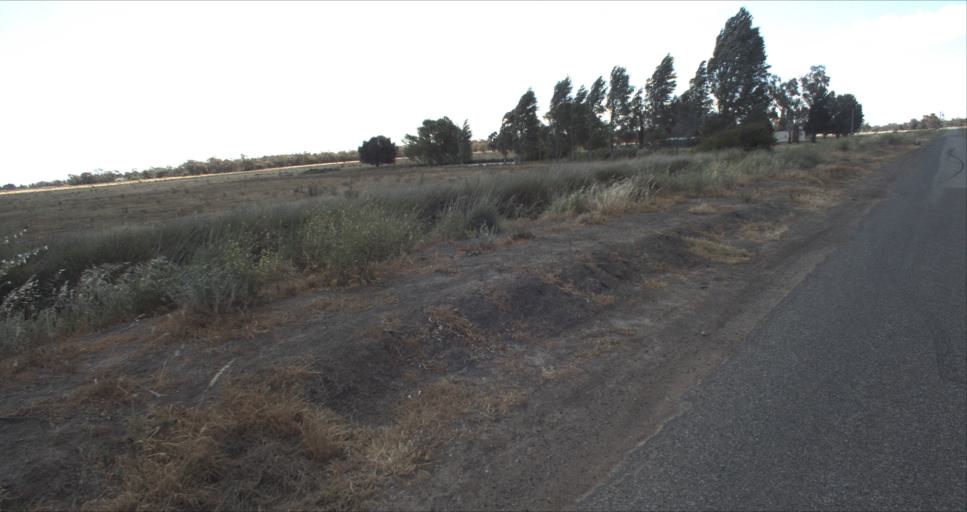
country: AU
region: New South Wales
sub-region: Leeton
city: Leeton
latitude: -34.5267
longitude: 146.2206
